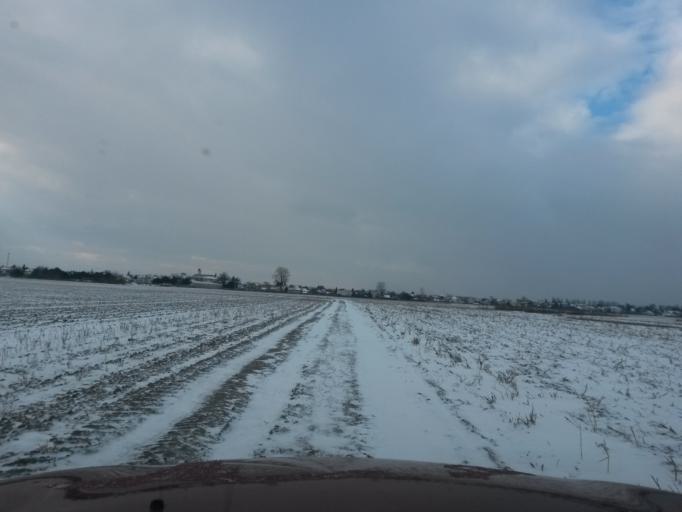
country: SK
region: Kosicky
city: Kosice
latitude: 48.6322
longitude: 21.3181
